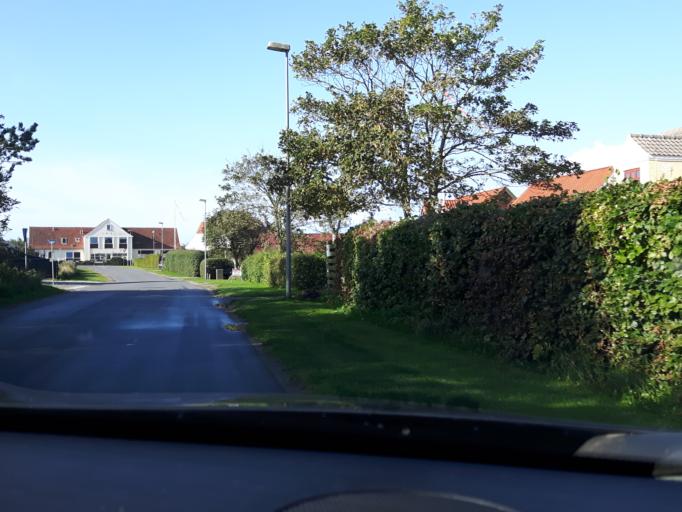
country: DK
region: North Denmark
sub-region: Hjorring Kommune
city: Hjorring
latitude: 57.4678
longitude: 9.8092
